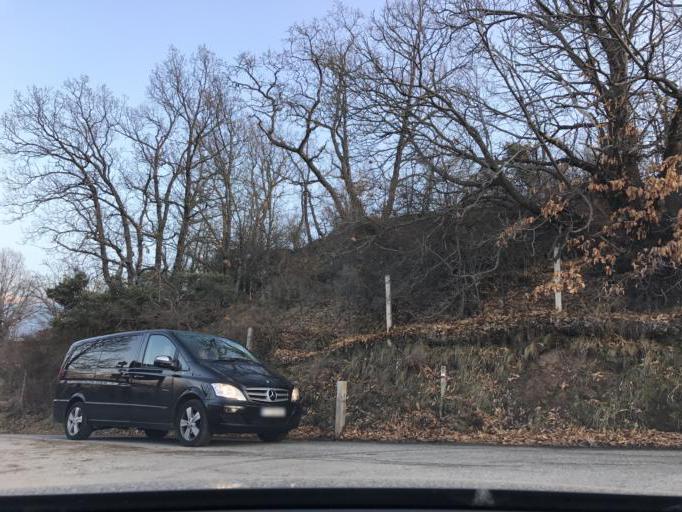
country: ES
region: Andalusia
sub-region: Provincia de Granada
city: Guejar-Sierra
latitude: 37.1372
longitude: -3.4177
